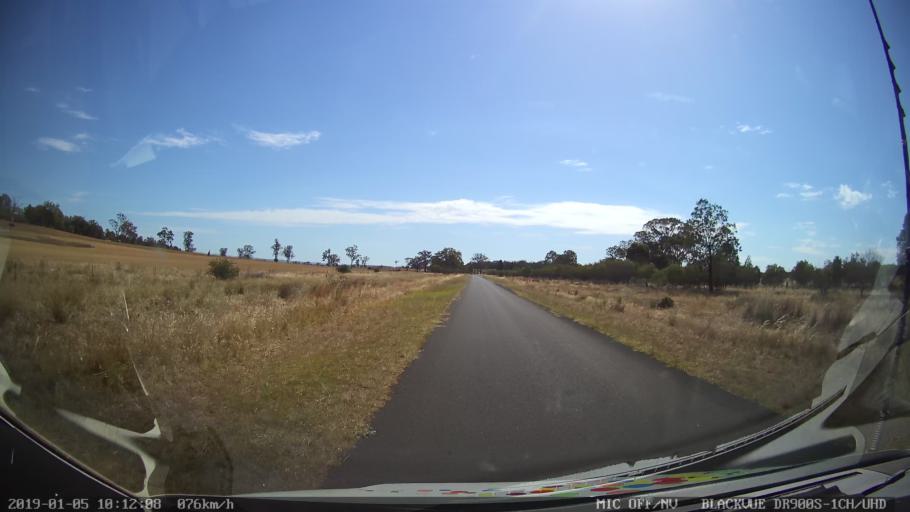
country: AU
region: New South Wales
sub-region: Gilgandra
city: Gilgandra
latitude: -31.6095
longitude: 148.9093
